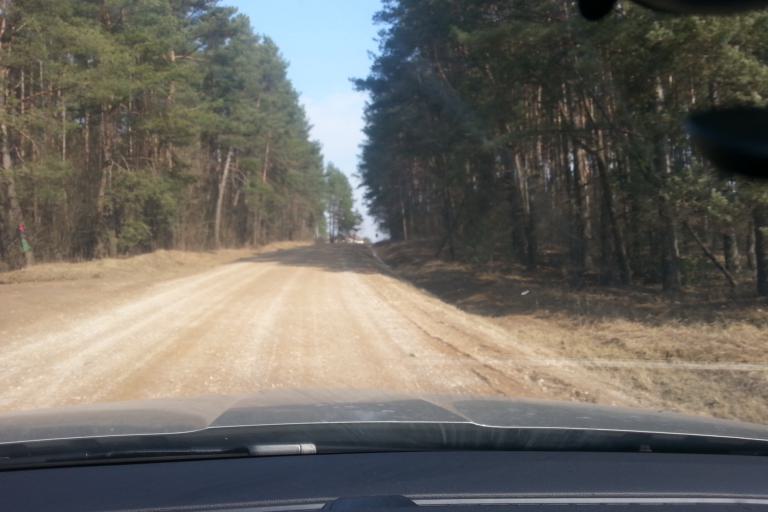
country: LT
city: Trakai
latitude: 54.5810
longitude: 24.9737
